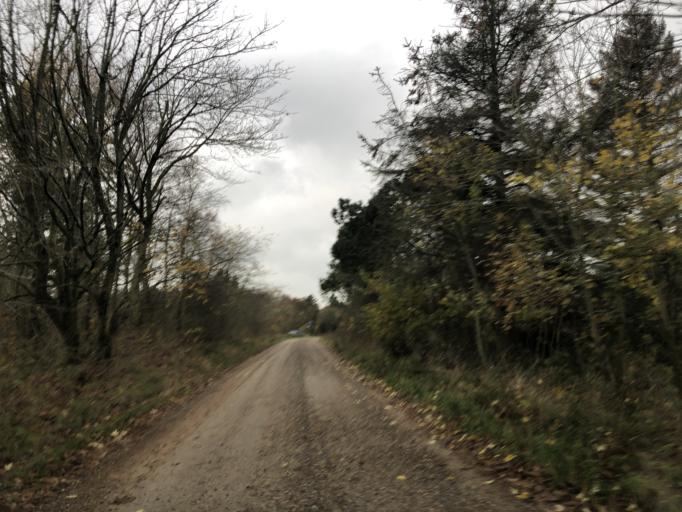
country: DK
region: Central Jutland
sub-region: Holstebro Kommune
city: Ulfborg
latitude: 56.3153
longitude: 8.2093
